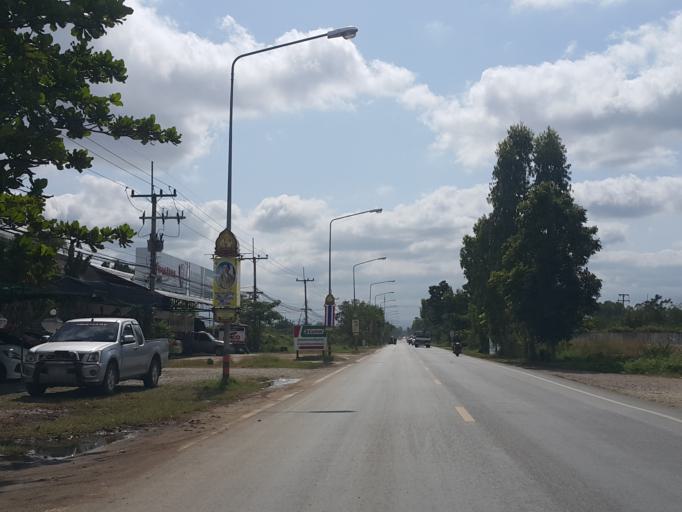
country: TH
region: Lamphun
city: Ban Thi
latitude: 18.5897
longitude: 99.0808
